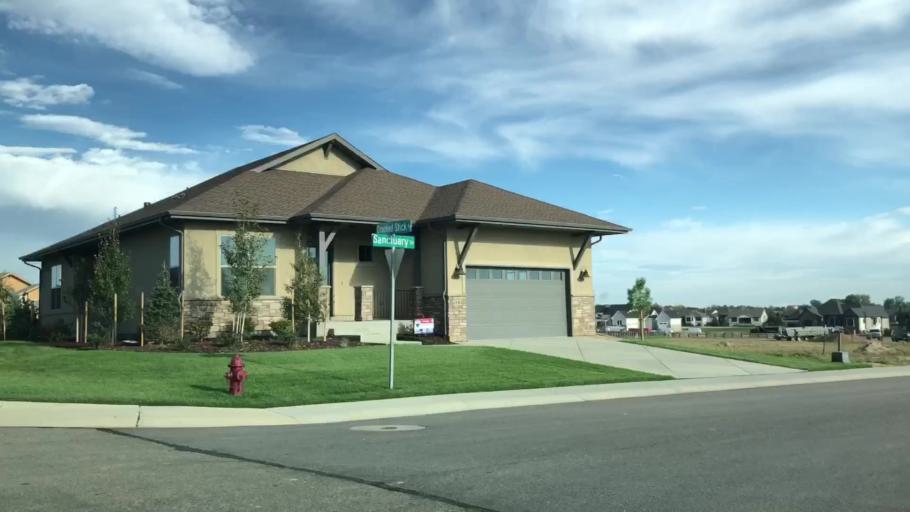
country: US
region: Colorado
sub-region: Weld County
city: Windsor
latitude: 40.4568
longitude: -104.9692
